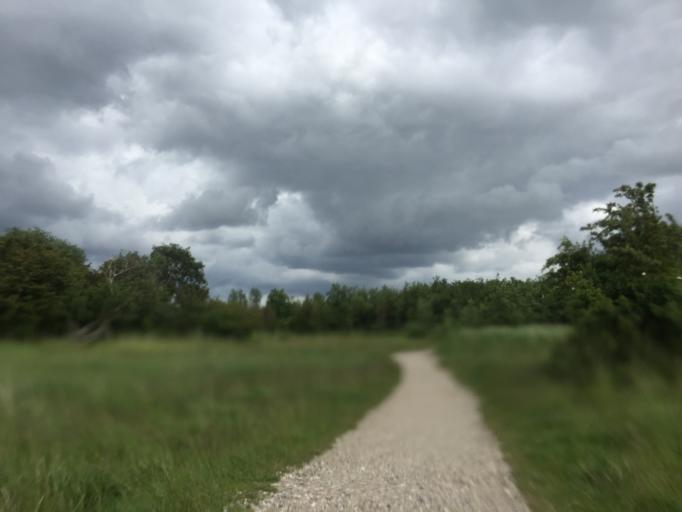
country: DK
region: Capital Region
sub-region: Tarnby Kommune
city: Tarnby
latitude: 55.6164
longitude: 12.5749
